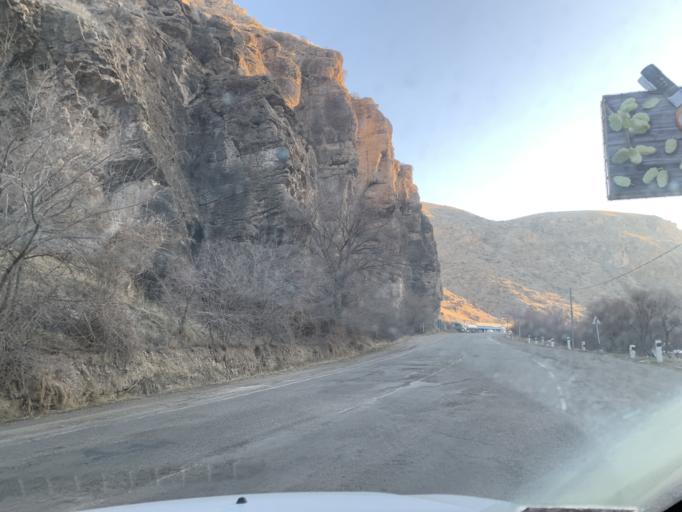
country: AM
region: Vayots' Dzori Marz
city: Areni
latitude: 39.7322
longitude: 45.2044
